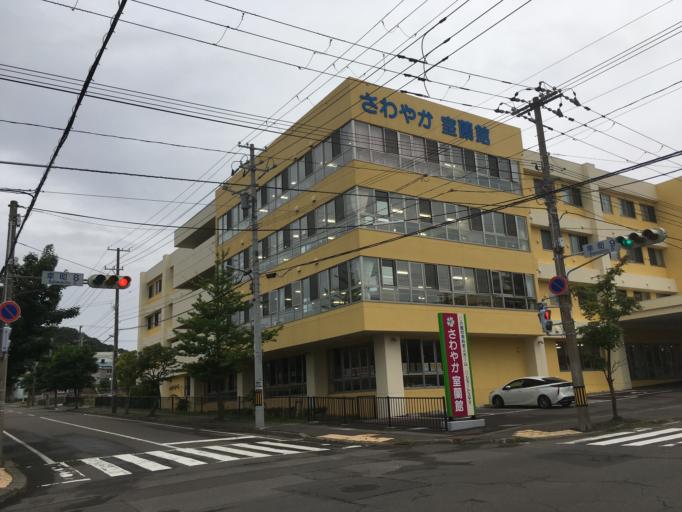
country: JP
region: Hokkaido
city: Muroran
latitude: 42.3151
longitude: 140.9700
